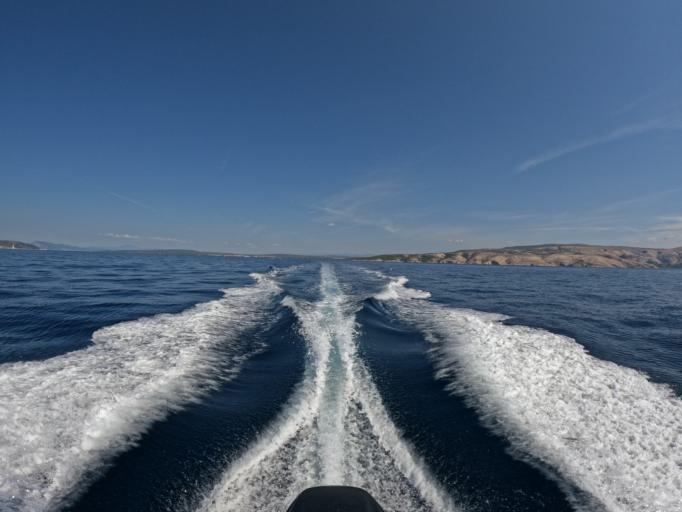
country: HR
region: Primorsko-Goranska
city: Punat
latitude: 44.9400
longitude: 14.6159
